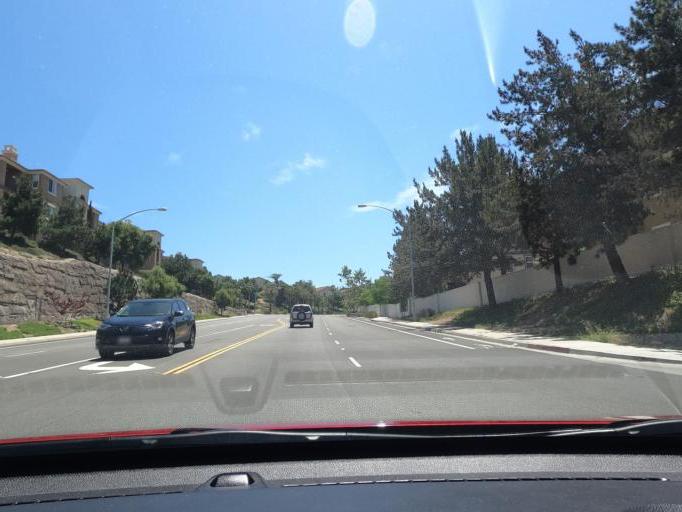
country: US
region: California
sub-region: San Diego County
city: Imperial Beach
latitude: 32.5735
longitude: -117.0375
